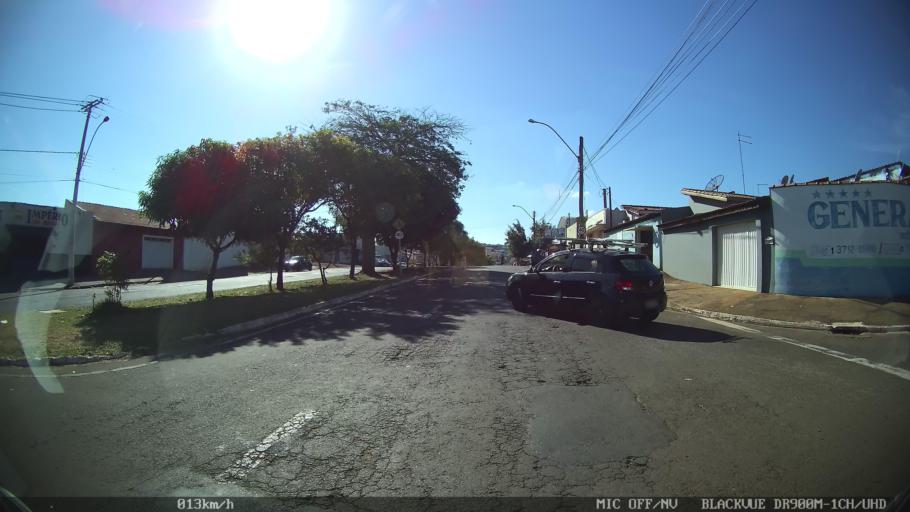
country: BR
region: Sao Paulo
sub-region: Franca
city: Franca
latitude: -20.4919
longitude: -47.4284
